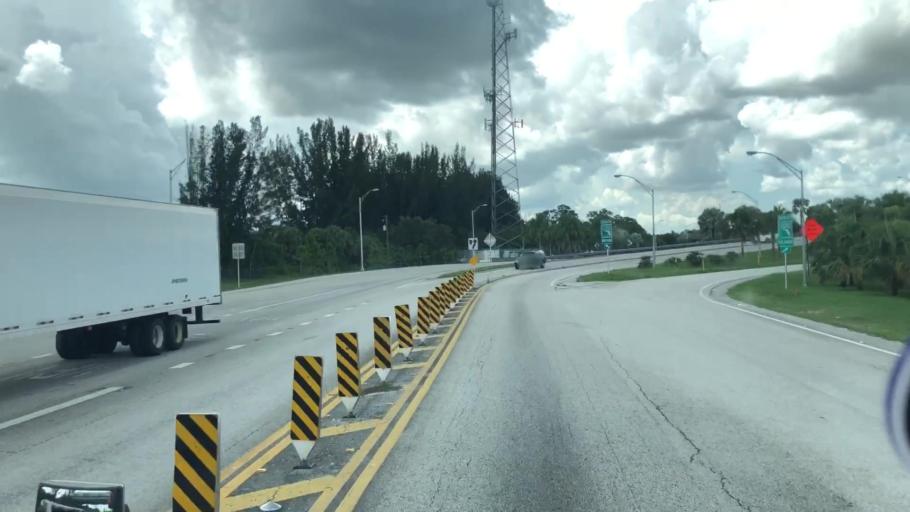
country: US
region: Florida
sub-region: Saint Lucie County
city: Fort Pierce South
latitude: 27.4101
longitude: -80.3988
